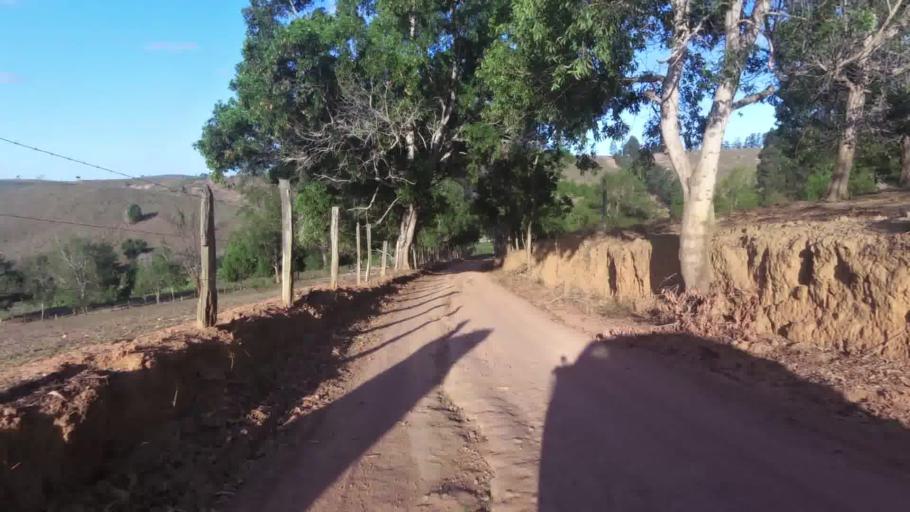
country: BR
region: Espirito Santo
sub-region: Marataizes
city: Marataizes
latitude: -21.1642
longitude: -41.0546
